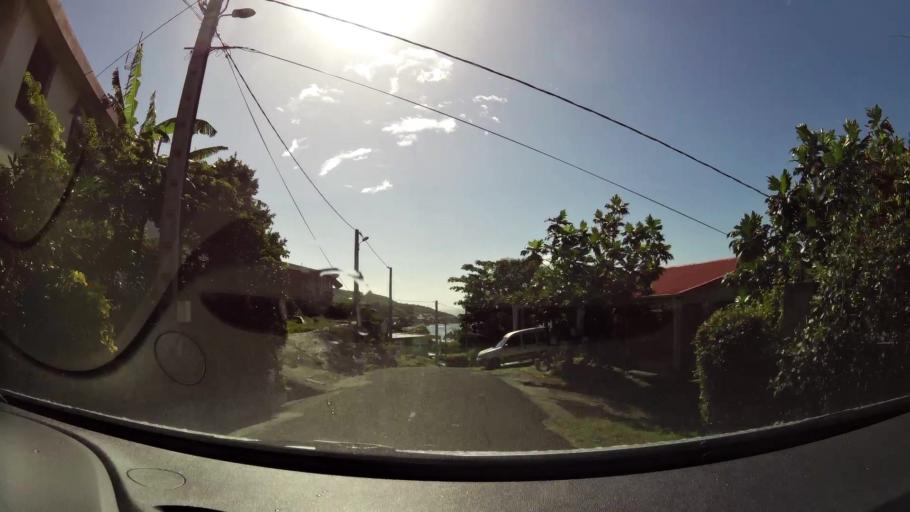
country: MQ
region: Martinique
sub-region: Martinique
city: Les Trois-Ilets
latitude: 14.4723
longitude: -61.0721
